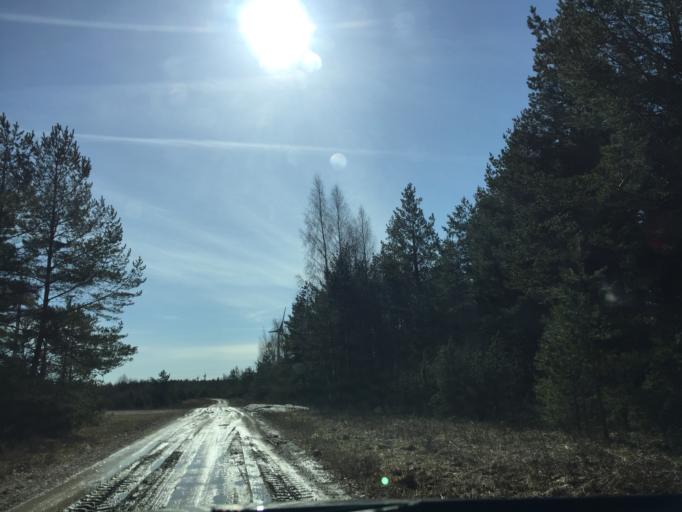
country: EE
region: Laeaene
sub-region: Haapsalu linn
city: Haapsalu
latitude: 58.6370
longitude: 23.5205
